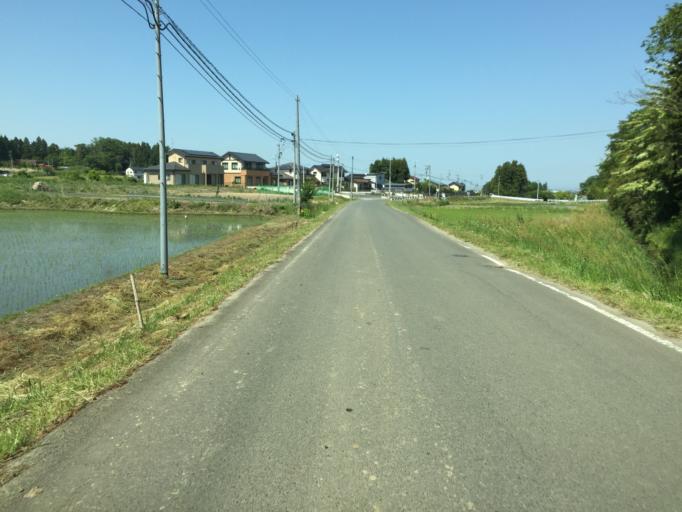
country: JP
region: Miyagi
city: Marumori
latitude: 37.8638
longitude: 140.9100
